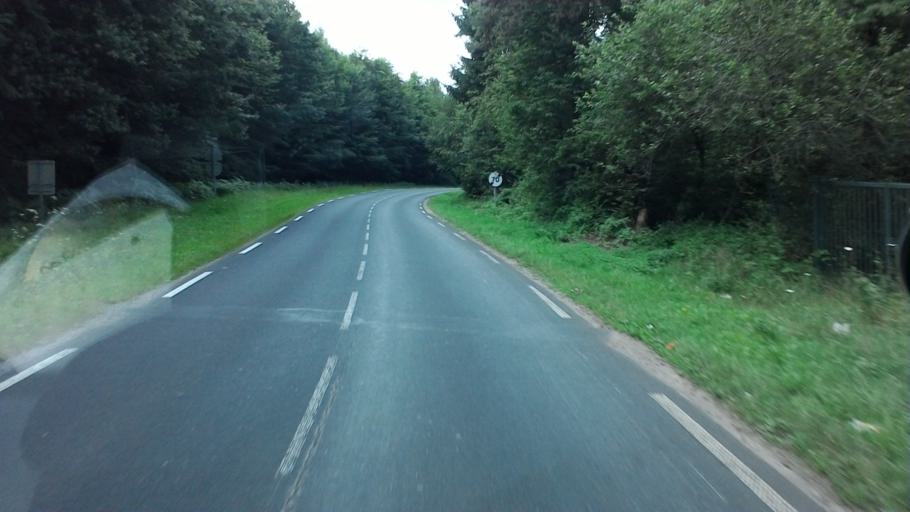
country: FR
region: Lorraine
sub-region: Departement des Vosges
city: Deyvillers
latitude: 48.1827
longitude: 6.4970
